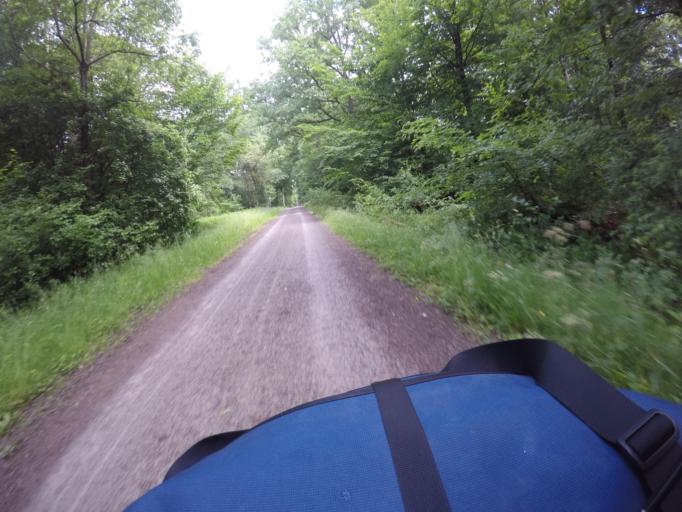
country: DE
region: Baden-Wuerttemberg
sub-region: Regierungsbezirk Stuttgart
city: Gerlingen
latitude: 48.7601
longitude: 9.0816
